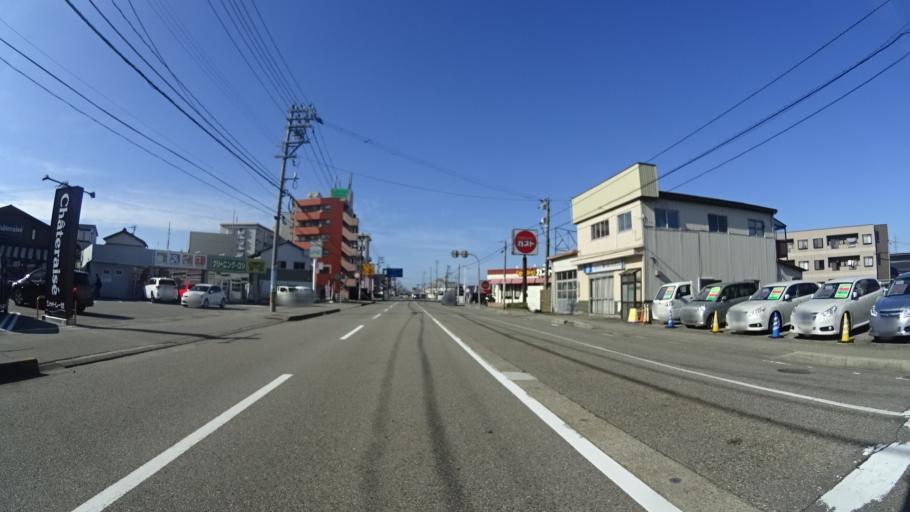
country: JP
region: Ishikawa
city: Kanazawa-shi
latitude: 36.5882
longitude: 136.6186
